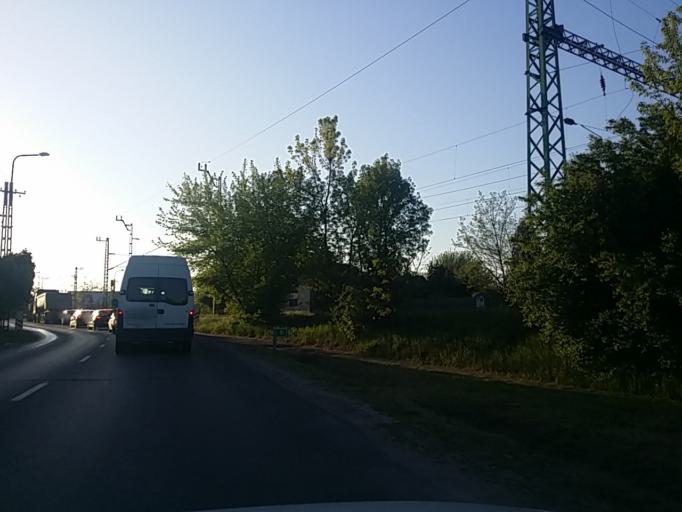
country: HU
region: Pest
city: Fot
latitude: 47.6117
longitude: 19.1825
